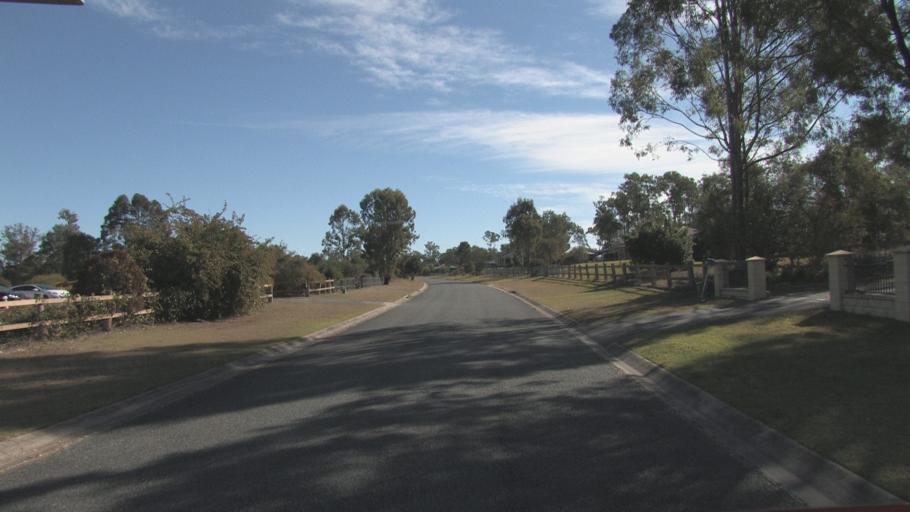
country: AU
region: Queensland
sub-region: Logan
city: North Maclean
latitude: -27.7981
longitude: 152.9690
